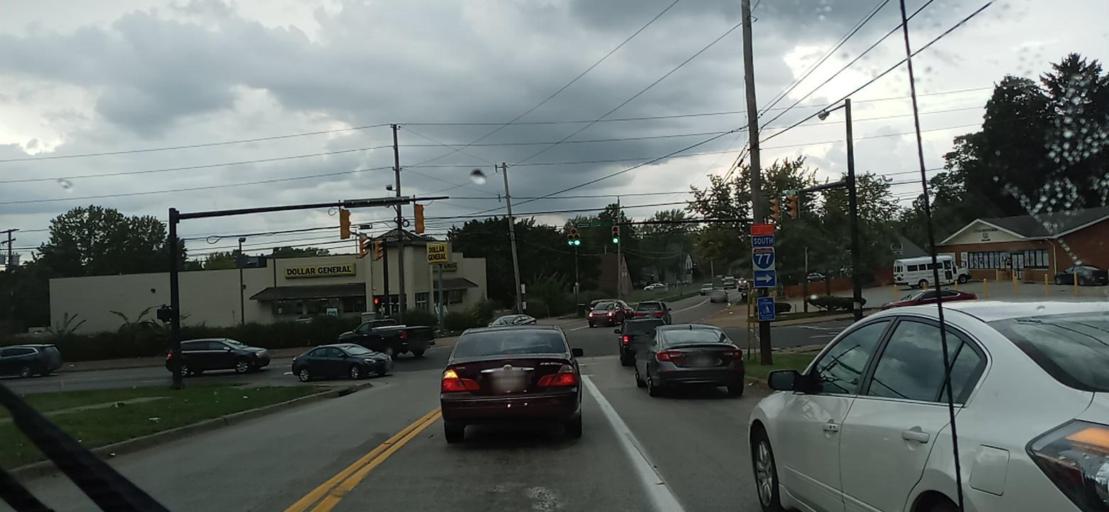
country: US
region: Ohio
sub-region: Summit County
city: Akron
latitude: 41.0674
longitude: -81.5589
